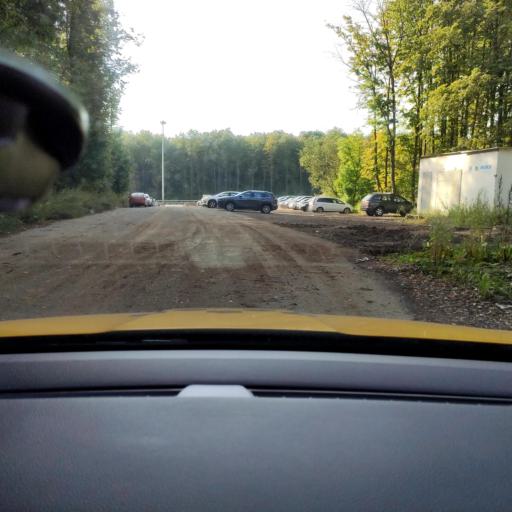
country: RU
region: Moskovskaya
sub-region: Leninskiy Rayon
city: Vnukovo
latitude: 55.5948
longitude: 37.2944
